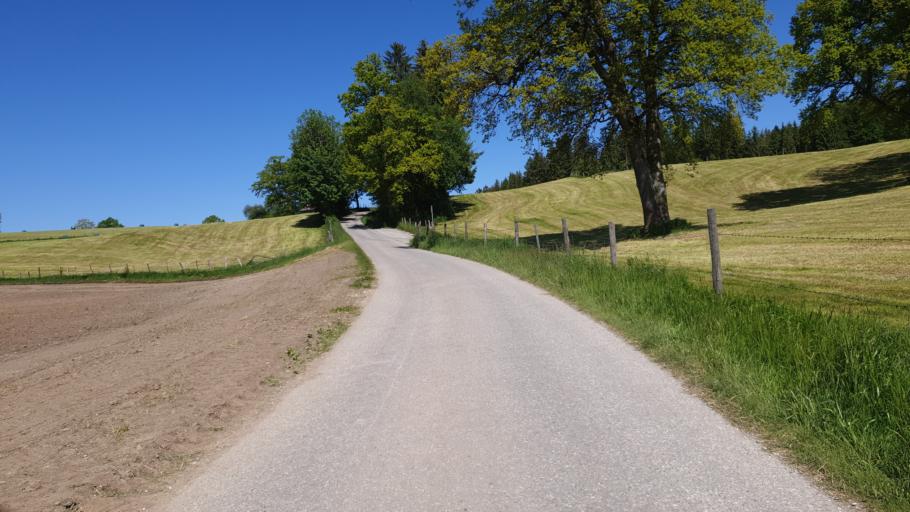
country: DE
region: Bavaria
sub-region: Upper Bavaria
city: Habach
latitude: 47.7587
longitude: 11.2774
